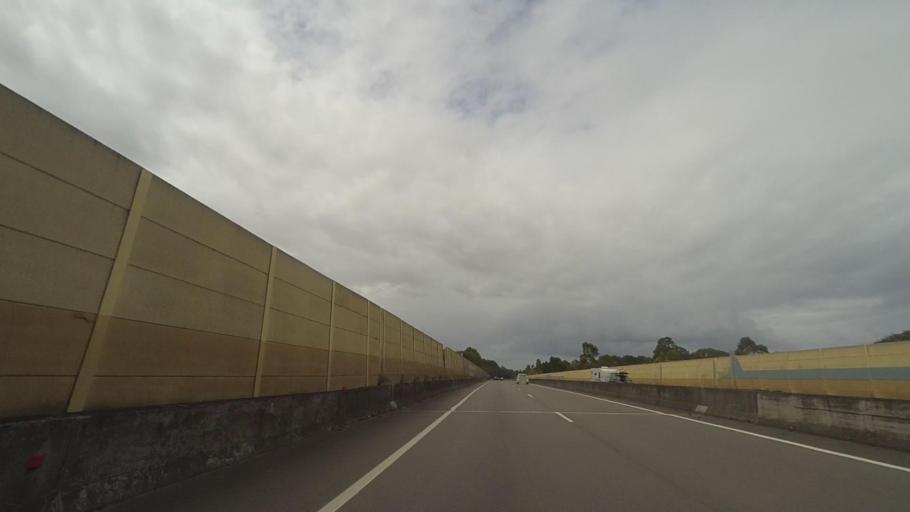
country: AU
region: New South Wales
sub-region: Port Stephens Shire
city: Raymond Terrace
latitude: -32.7557
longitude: 151.7654
